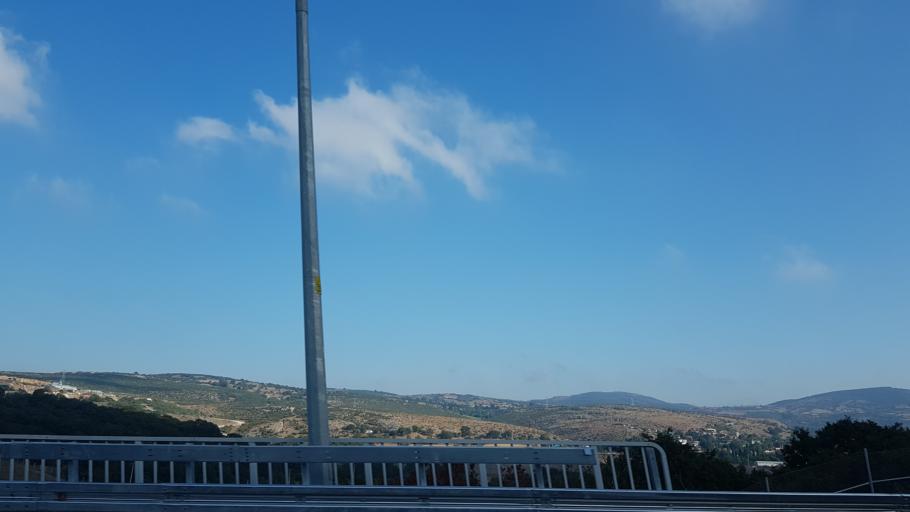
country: TR
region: Balikesir
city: Yenikoy
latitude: 39.7659
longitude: 28.0024
